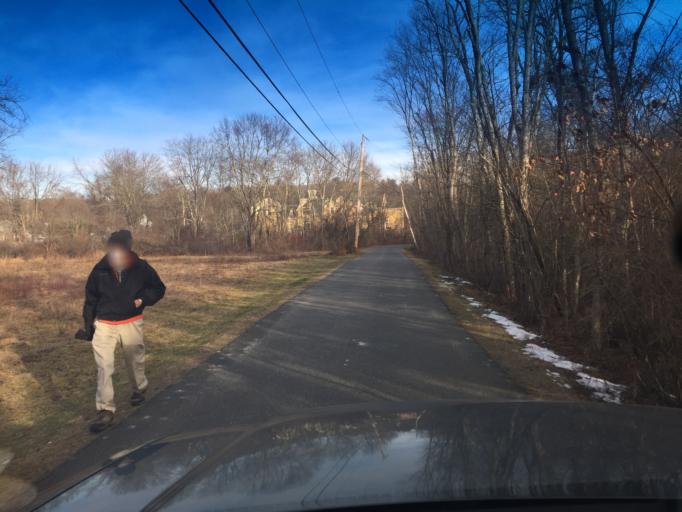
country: US
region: Massachusetts
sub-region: Middlesex County
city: Sherborn
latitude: 42.2454
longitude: -71.3711
